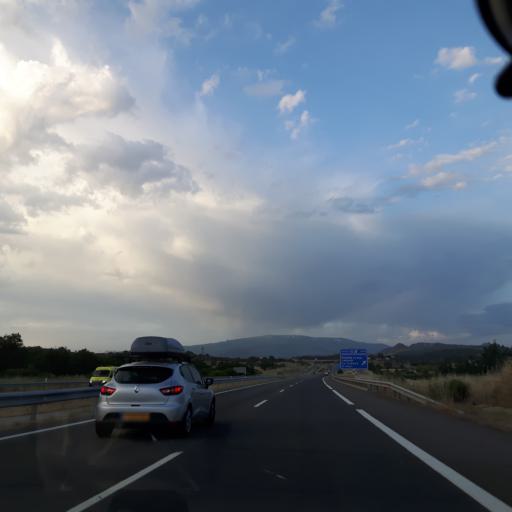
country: ES
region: Castille and Leon
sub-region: Provincia de Salamanca
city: Fuentes de Bejar
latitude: 40.5125
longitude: -5.6742
